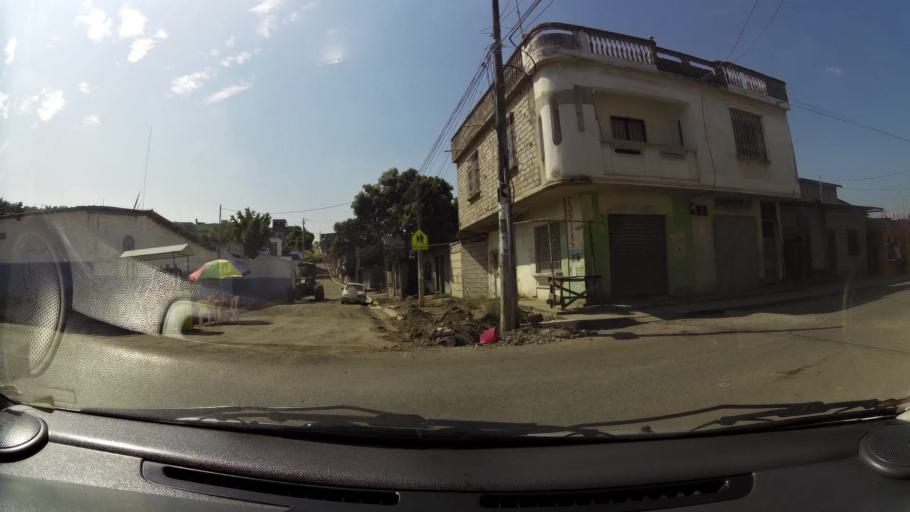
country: EC
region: Guayas
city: Eloy Alfaro
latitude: -2.1193
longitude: -79.9132
